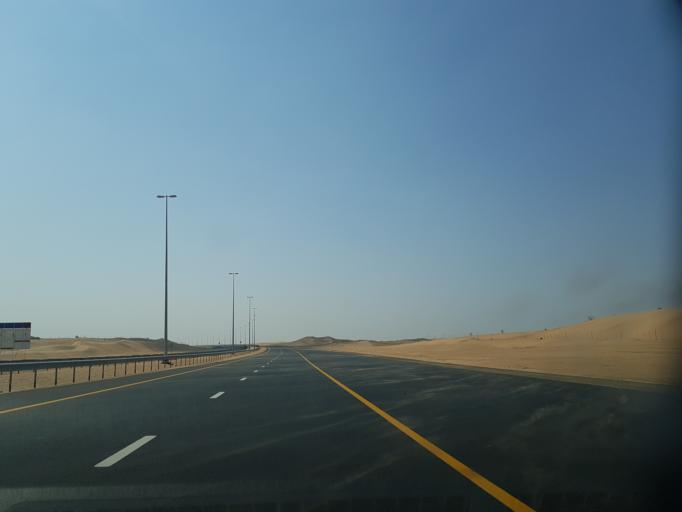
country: AE
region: Ash Shariqah
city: Adh Dhayd
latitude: 25.2692
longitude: 55.6529
